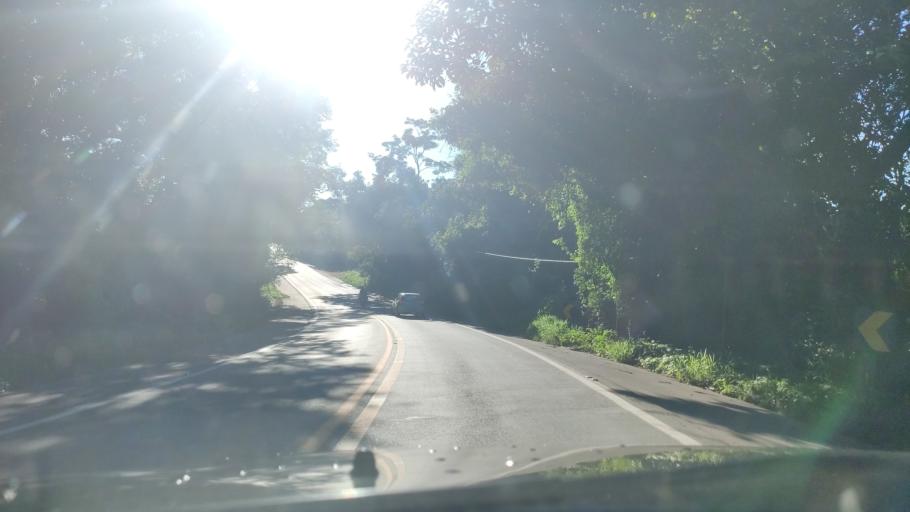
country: BR
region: Sao Paulo
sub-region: Socorro
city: Socorro
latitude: -22.5528
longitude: -46.5668
